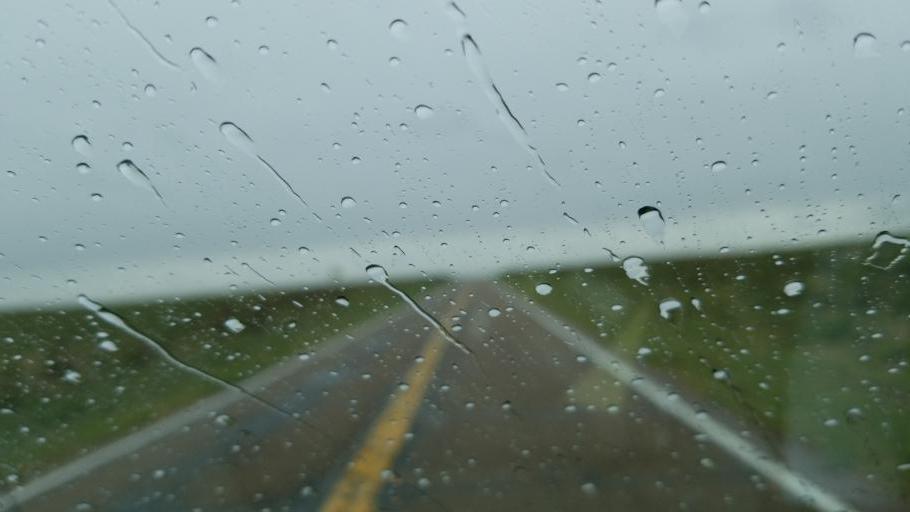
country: US
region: Colorado
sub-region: Lincoln County
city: Hugo
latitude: 38.8495
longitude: -103.1682
